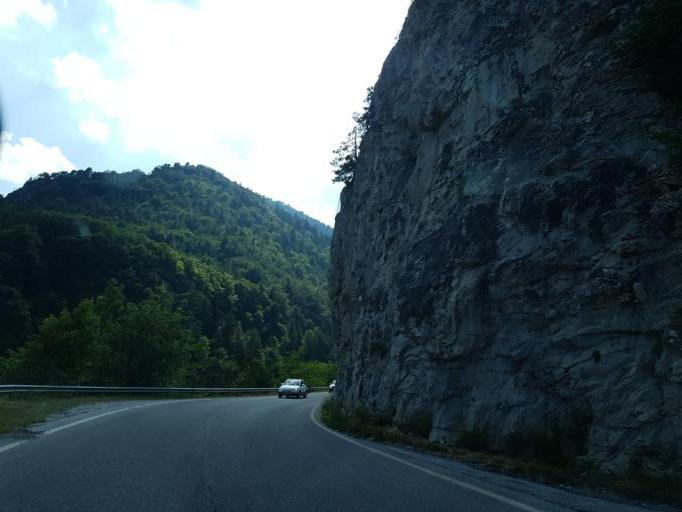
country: IT
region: Piedmont
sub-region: Provincia di Cuneo
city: Macra
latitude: 44.4995
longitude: 7.1729
